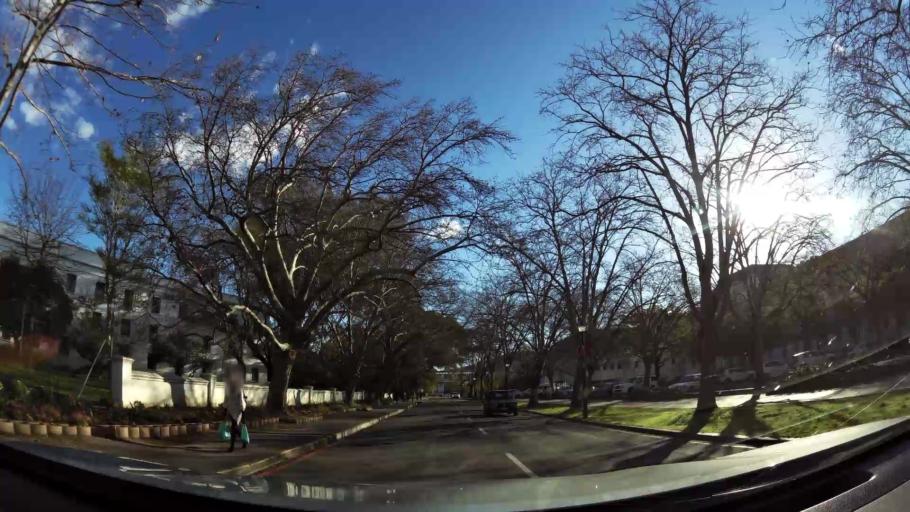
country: ZA
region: Western Cape
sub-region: Cape Winelands District Municipality
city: Stellenbosch
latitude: -33.9341
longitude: 18.8640
